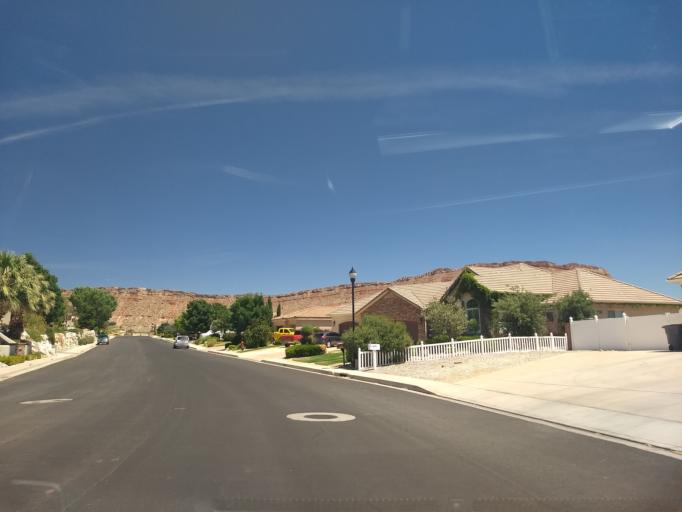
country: US
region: Utah
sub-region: Washington County
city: Washington
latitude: 37.0877
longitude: -113.4867
